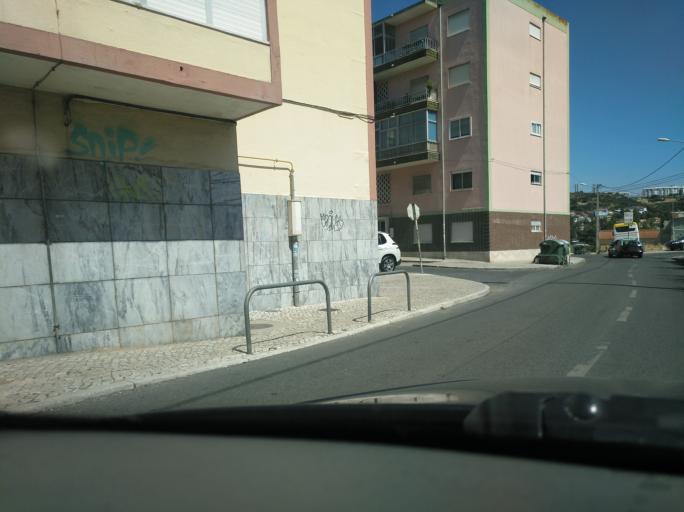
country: PT
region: Lisbon
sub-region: Odivelas
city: Odivelas
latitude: 38.7857
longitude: -9.1834
